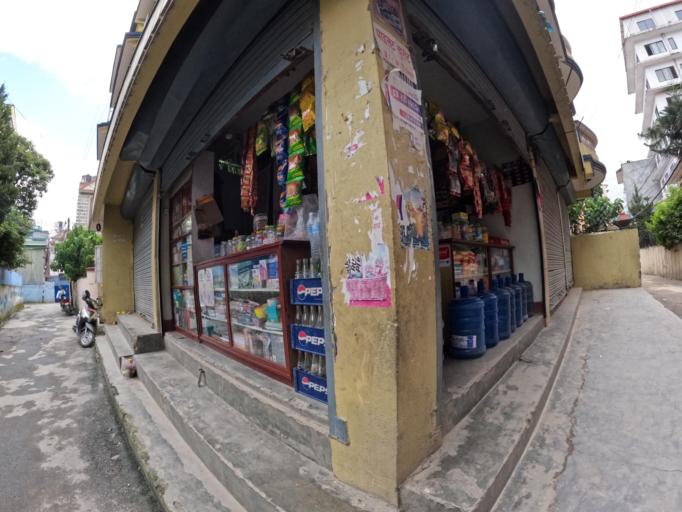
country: NP
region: Central Region
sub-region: Bagmati Zone
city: Kathmandu
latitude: 27.7391
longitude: 85.3118
